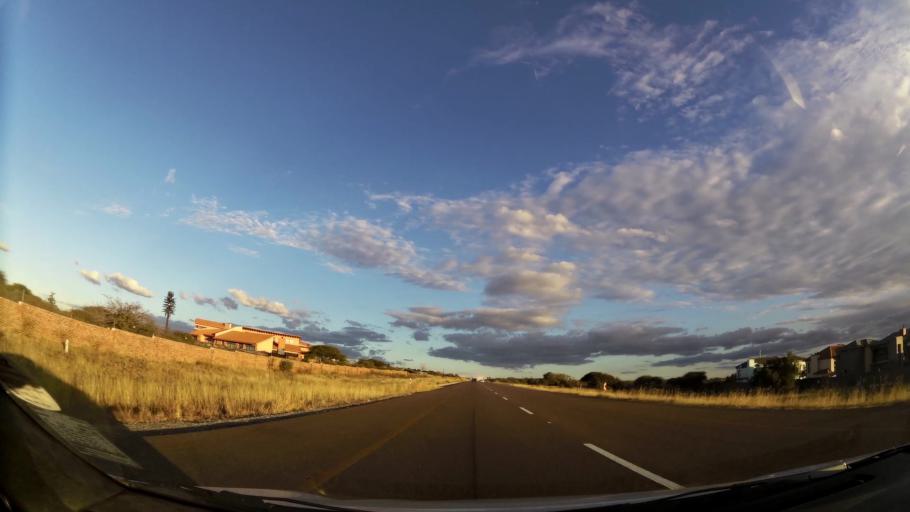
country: ZA
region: Limpopo
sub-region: Capricorn District Municipality
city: Polokwane
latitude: -23.8637
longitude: 29.5064
